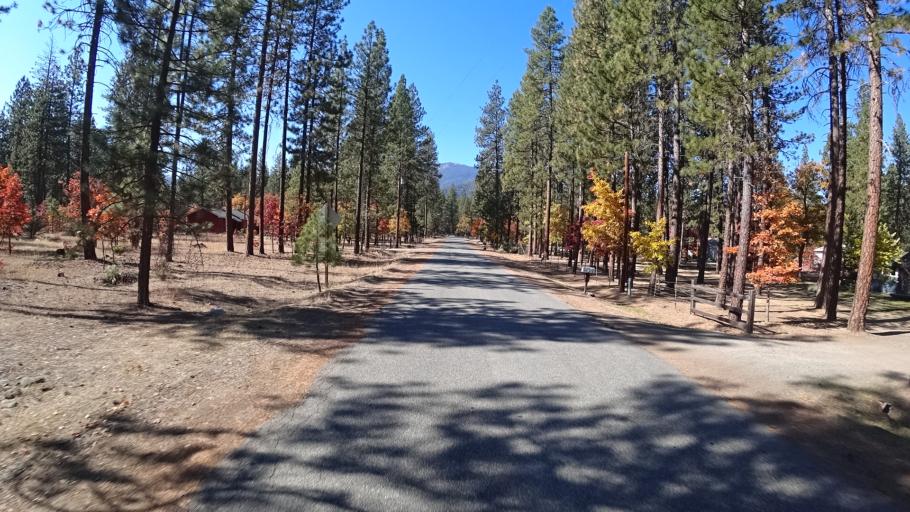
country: US
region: California
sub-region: Siskiyou County
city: Yreka
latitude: 41.6035
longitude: -122.9717
